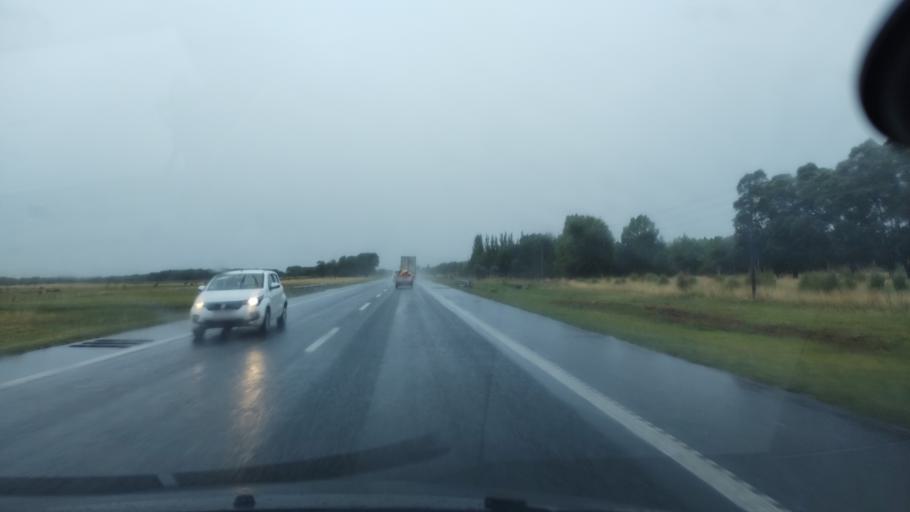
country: AR
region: Buenos Aires
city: Canuelas
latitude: -35.0637
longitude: -58.8183
